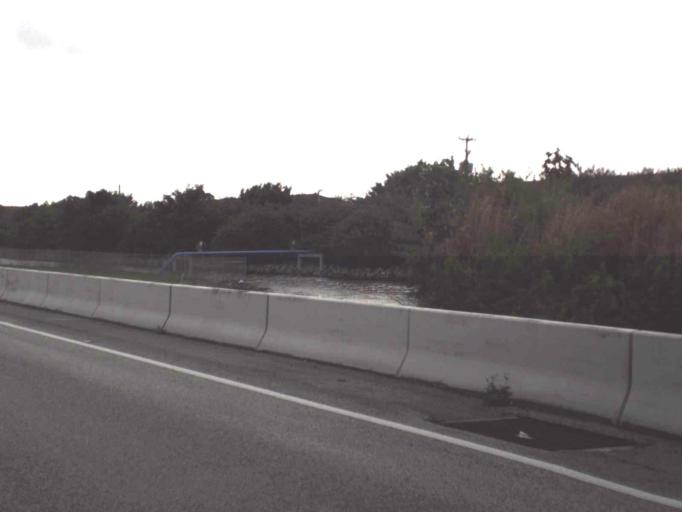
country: US
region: Florida
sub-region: Miami-Dade County
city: Lake Lucerne
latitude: 25.9652
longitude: -80.2296
